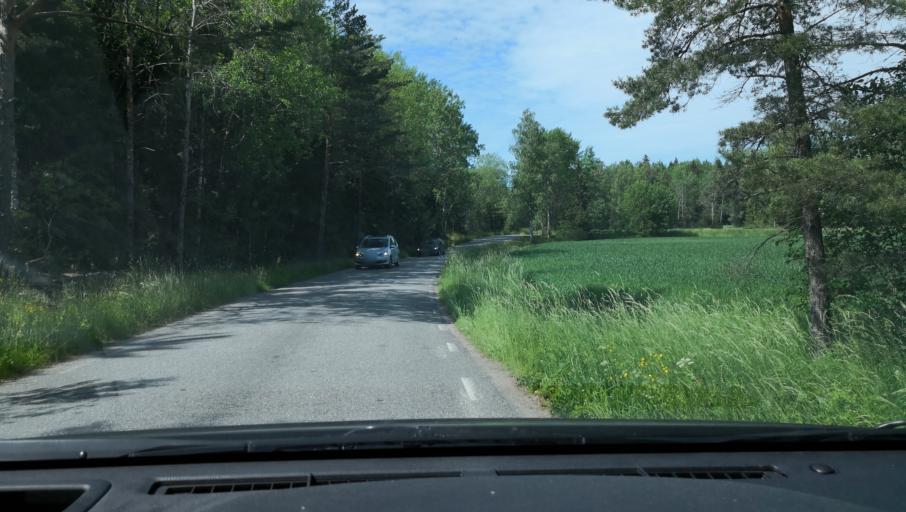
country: SE
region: Stockholm
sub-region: Sigtuna Kommun
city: Sigtuna
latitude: 59.6866
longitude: 17.6695
